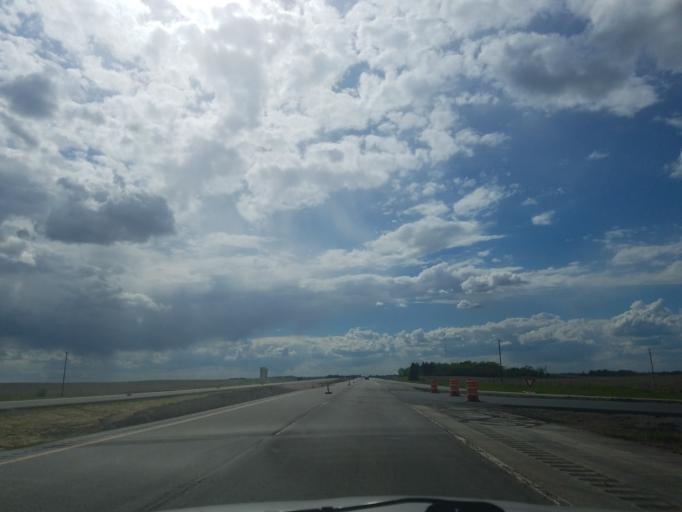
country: US
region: North Dakota
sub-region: Barnes County
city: Valley City
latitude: 46.9201
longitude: -97.7900
